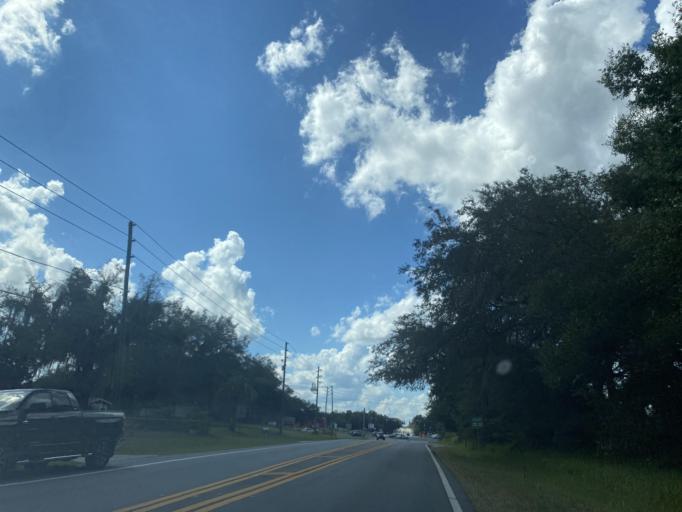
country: US
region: Florida
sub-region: Sumter County
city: The Villages
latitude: 28.9820
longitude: -81.9851
